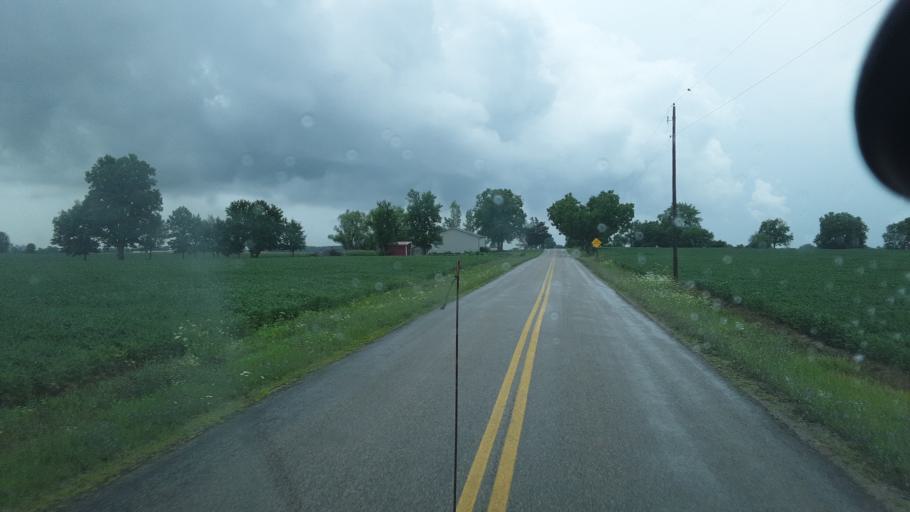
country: US
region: Ohio
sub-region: Williams County
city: Edgerton
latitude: 41.5685
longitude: -84.7885
